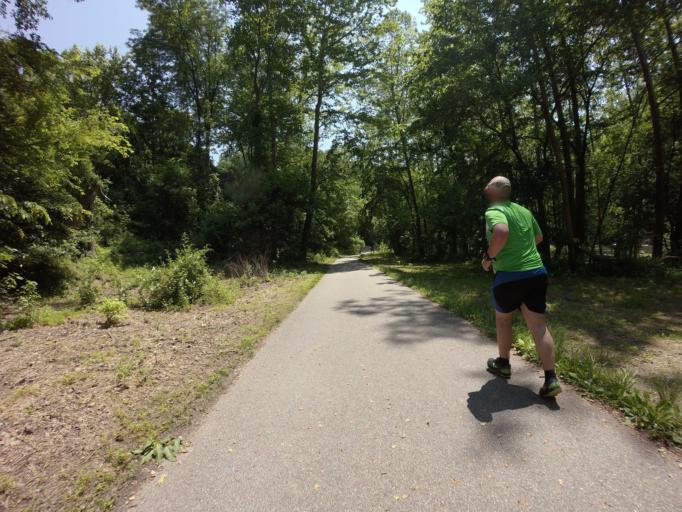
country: US
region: Maryland
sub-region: Howard County
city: Ilchester
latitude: 39.2457
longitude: -76.7529
